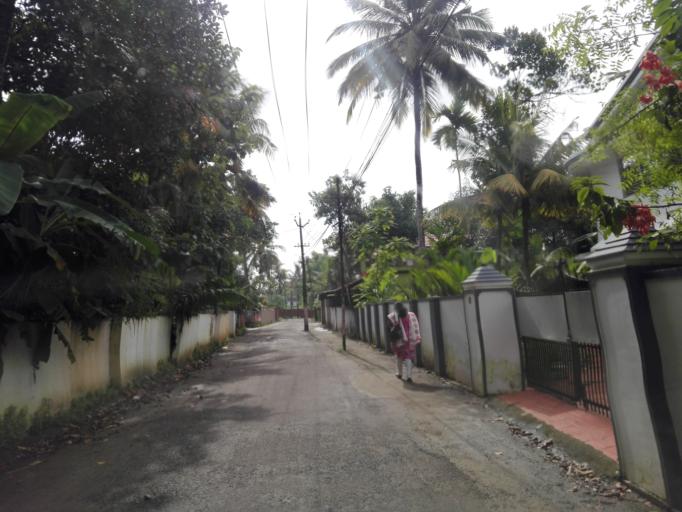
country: IN
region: Kerala
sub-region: Kottayam
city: Vaikam
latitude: 9.7817
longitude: 76.3931
